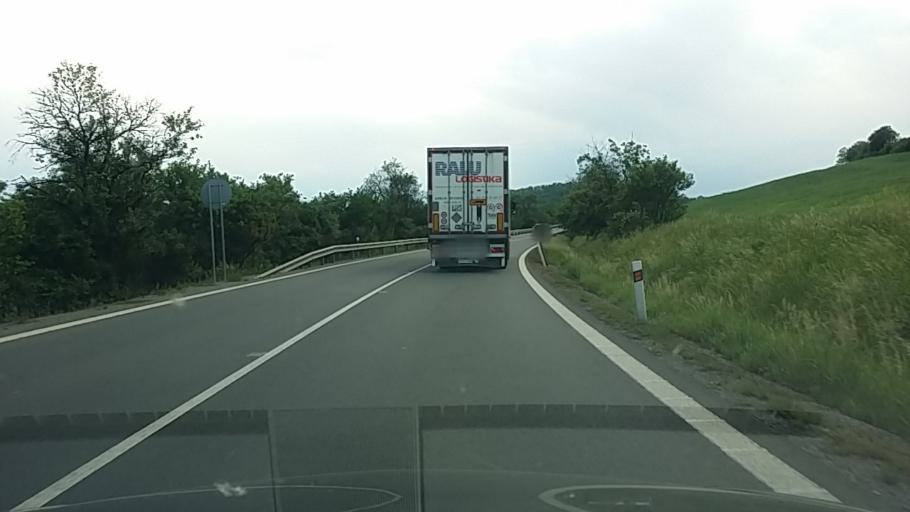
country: SK
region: Banskobystricky
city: Krupina
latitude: 48.3236
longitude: 19.0582
